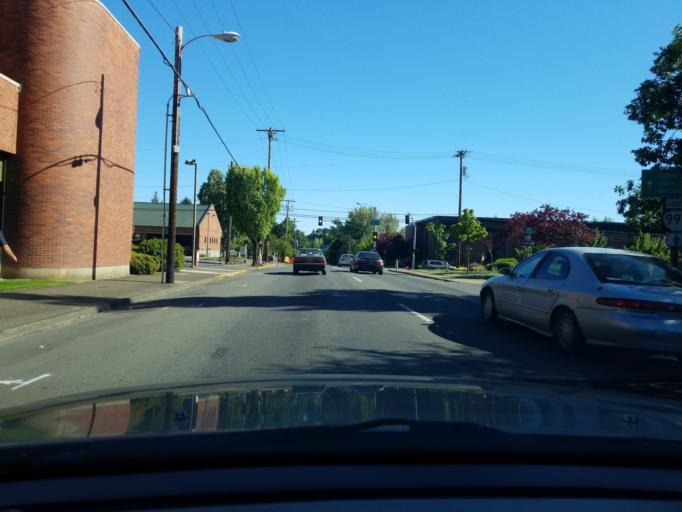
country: US
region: Oregon
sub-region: Yamhill County
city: McMinnville
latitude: 45.2099
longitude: -123.1991
